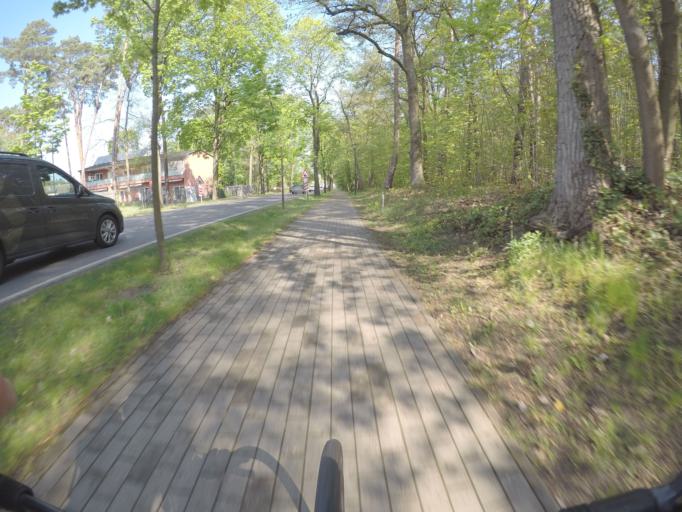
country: DE
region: Brandenburg
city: Wandlitz
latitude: 52.7179
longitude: 13.4364
